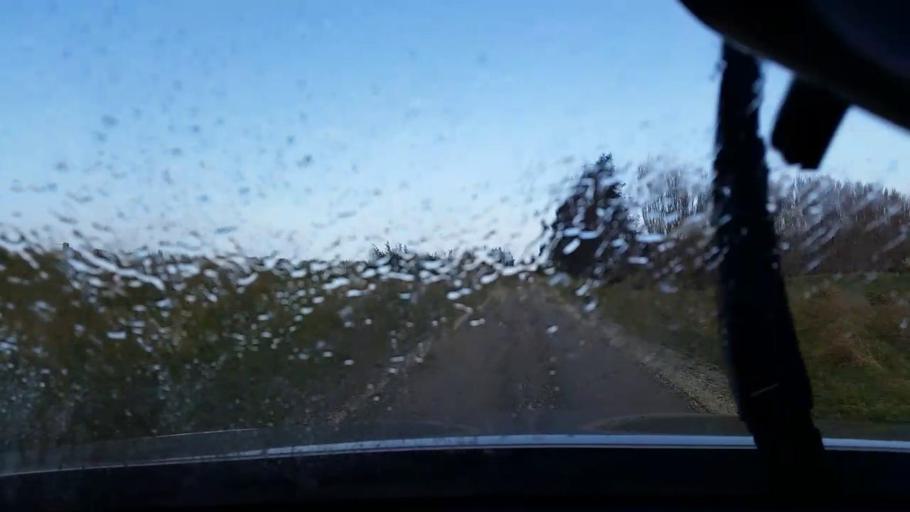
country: NZ
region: Southland
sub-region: Southland District
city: Winton
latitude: -46.2759
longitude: 168.2927
